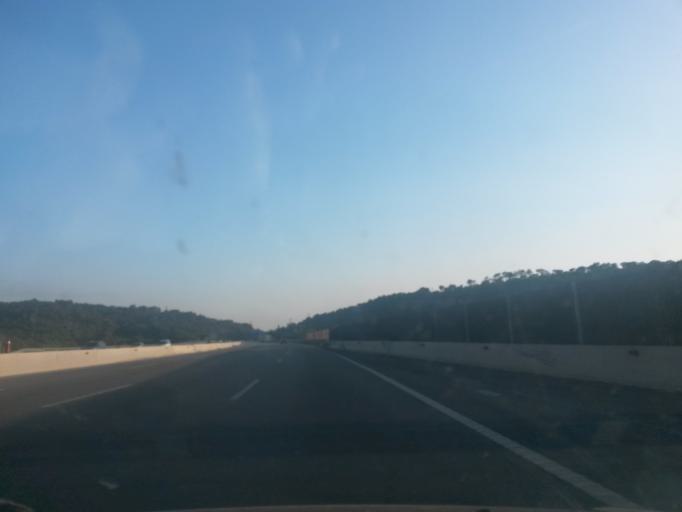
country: ES
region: Catalonia
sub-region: Provincia de Girona
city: Sarria de Ter
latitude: 42.0100
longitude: 2.8093
